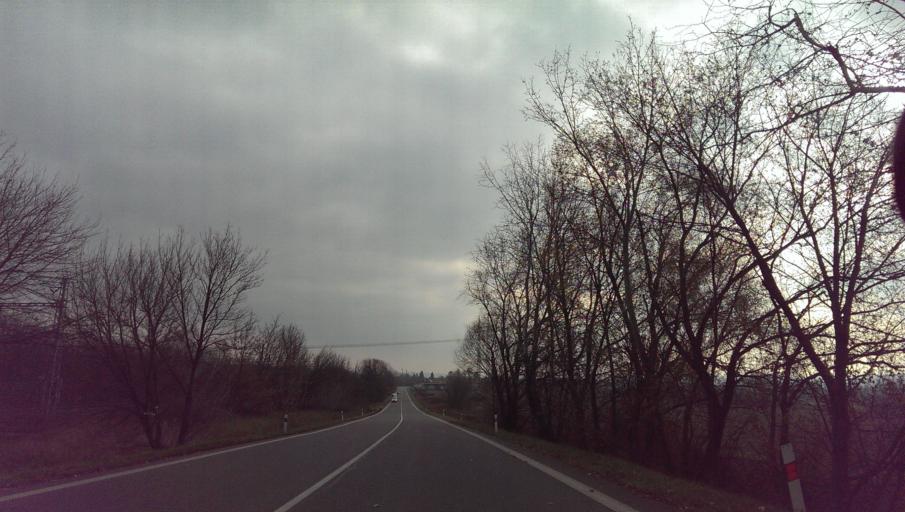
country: CZ
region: Zlin
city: Tlumacov
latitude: 49.2672
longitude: 17.4917
